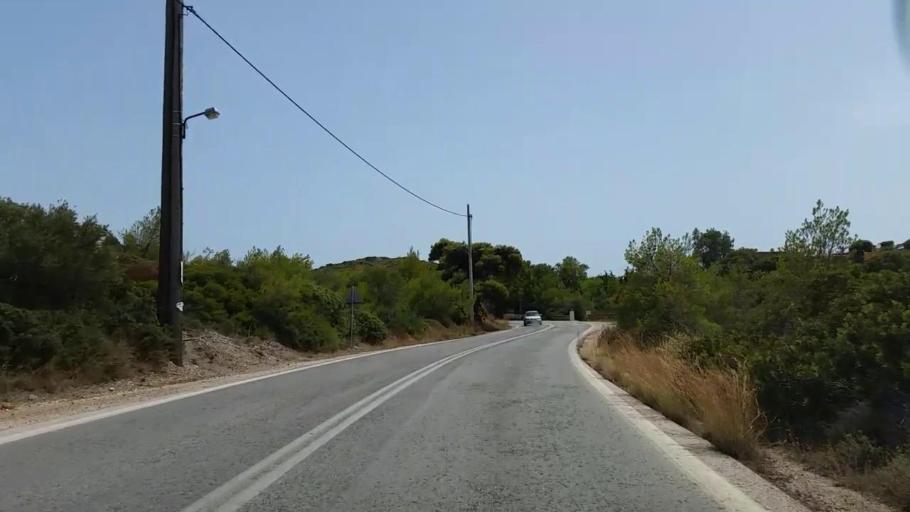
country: GR
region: Attica
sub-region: Nomarchia Anatolikis Attikis
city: Lavrio
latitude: 37.6578
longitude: 24.0294
